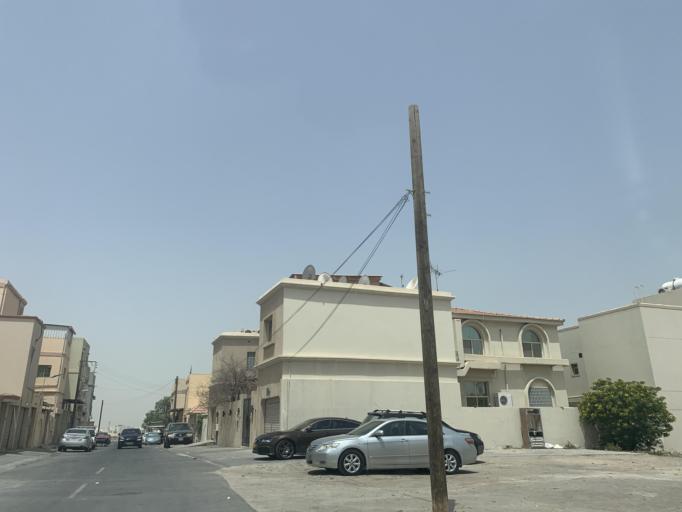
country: BH
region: Central Governorate
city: Madinat Hamad
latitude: 26.1506
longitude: 50.5184
